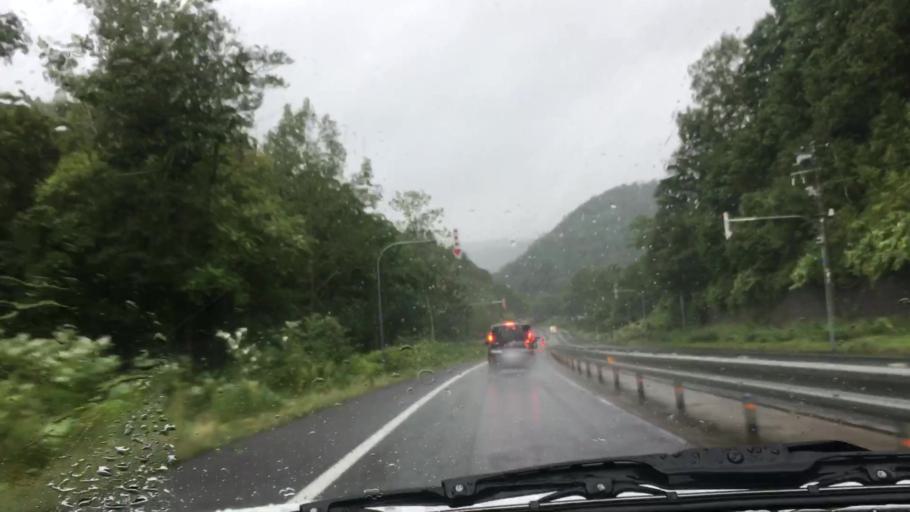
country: JP
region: Hokkaido
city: Otaru
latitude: 42.8447
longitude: 141.0585
